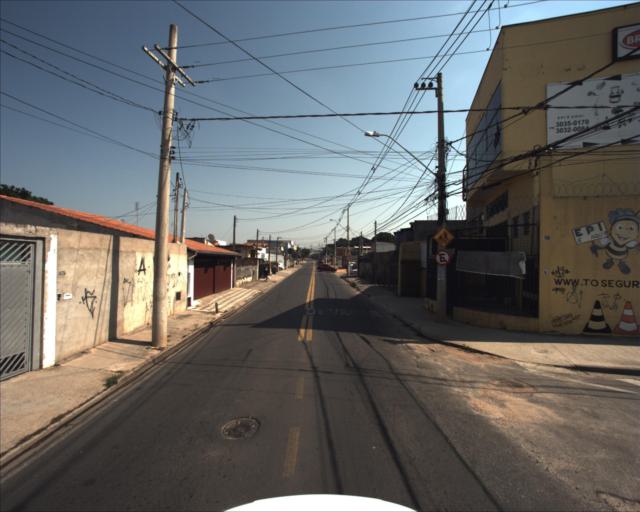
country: BR
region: Sao Paulo
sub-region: Sorocaba
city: Sorocaba
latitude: -23.4604
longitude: -47.4818
